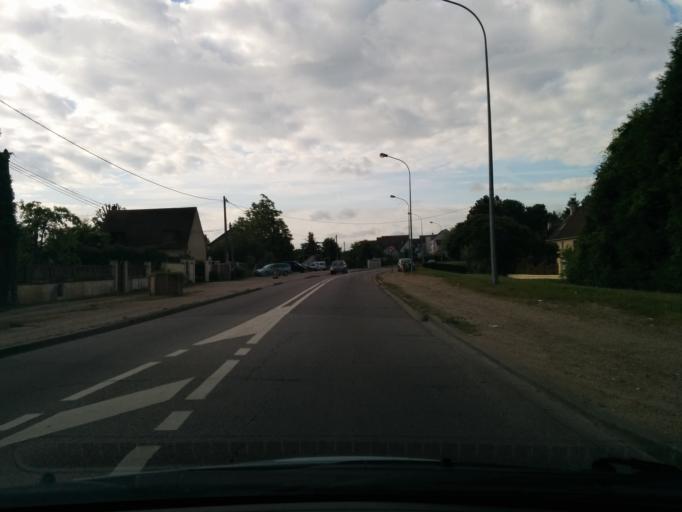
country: FR
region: Ile-de-France
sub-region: Departement des Yvelines
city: Mantes-la-Jolie
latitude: 48.9965
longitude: 1.7248
